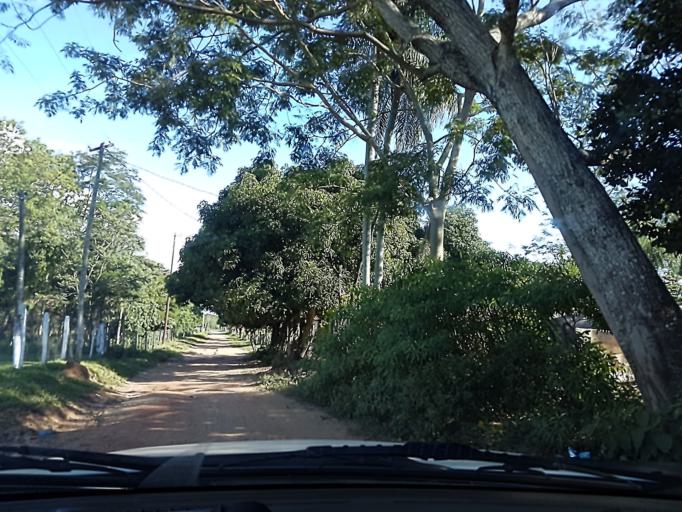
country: PY
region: Cordillera
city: Arroyos y Esteros
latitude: -24.9817
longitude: -57.1991
